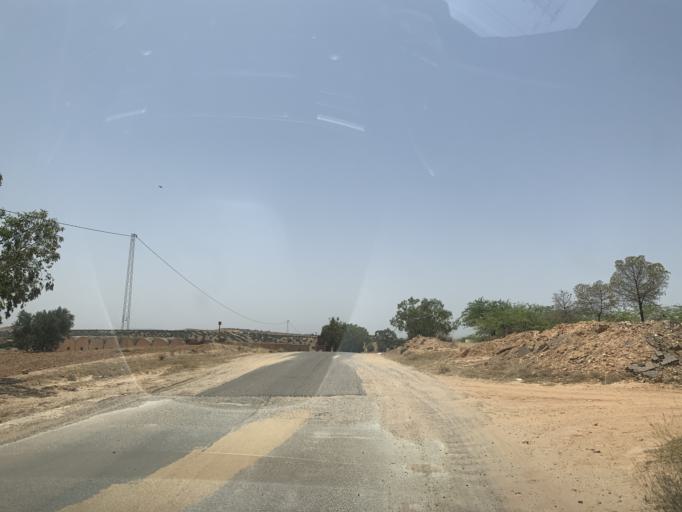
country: TN
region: Al Mahdiyah
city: Shurban
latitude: 35.1607
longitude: 10.2522
